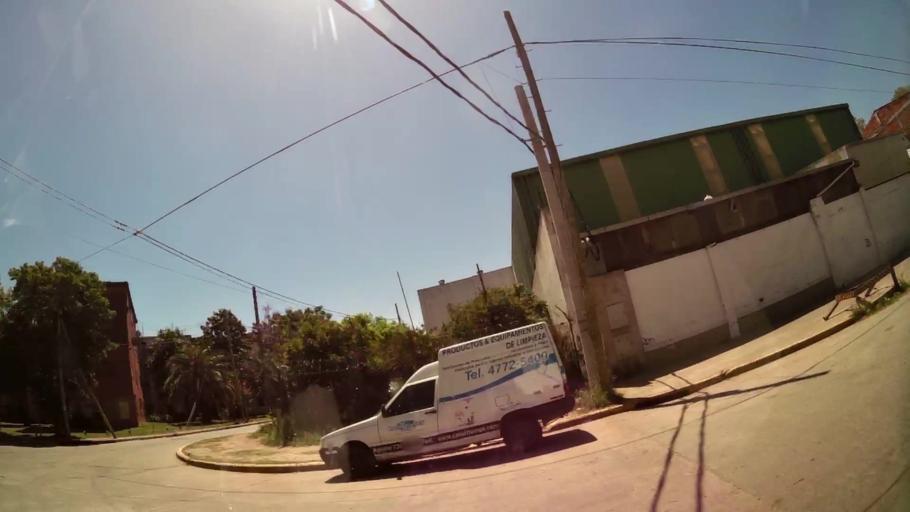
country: AR
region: Buenos Aires
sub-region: Partido de Tigre
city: Tigre
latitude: -34.4836
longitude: -58.6515
